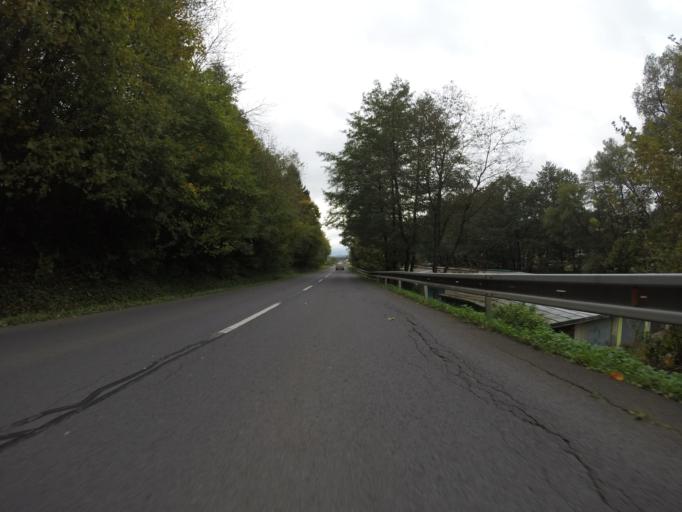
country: SK
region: Banskobystricky
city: Hrinova
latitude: 48.5766
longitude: 19.5318
